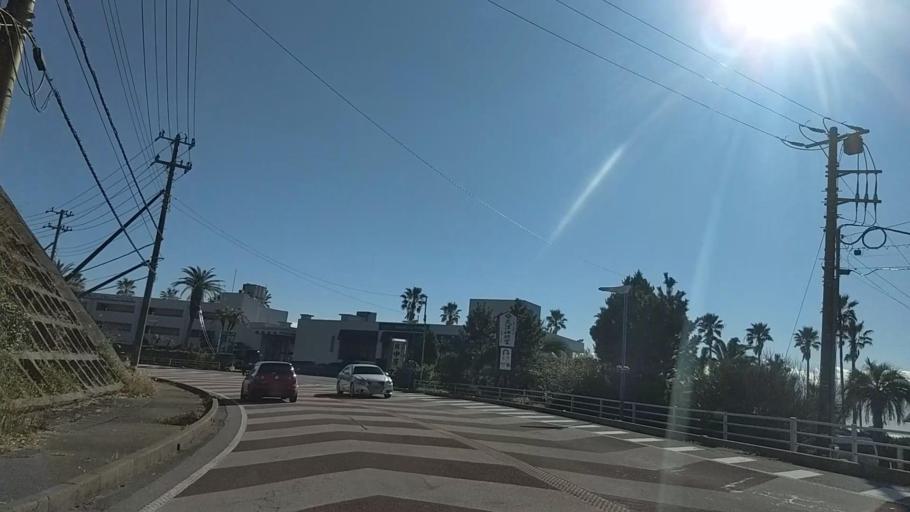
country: JP
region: Chiba
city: Kawaguchi
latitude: 35.1215
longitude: 140.1730
